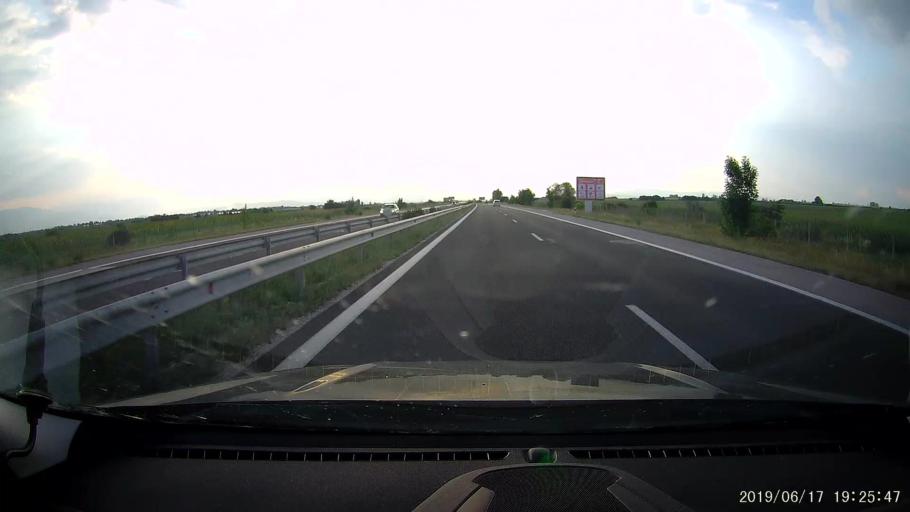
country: BG
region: Pazardzhik
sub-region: Obshtina Pazardzhik
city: Pazardzhik
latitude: 42.2497
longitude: 24.3461
